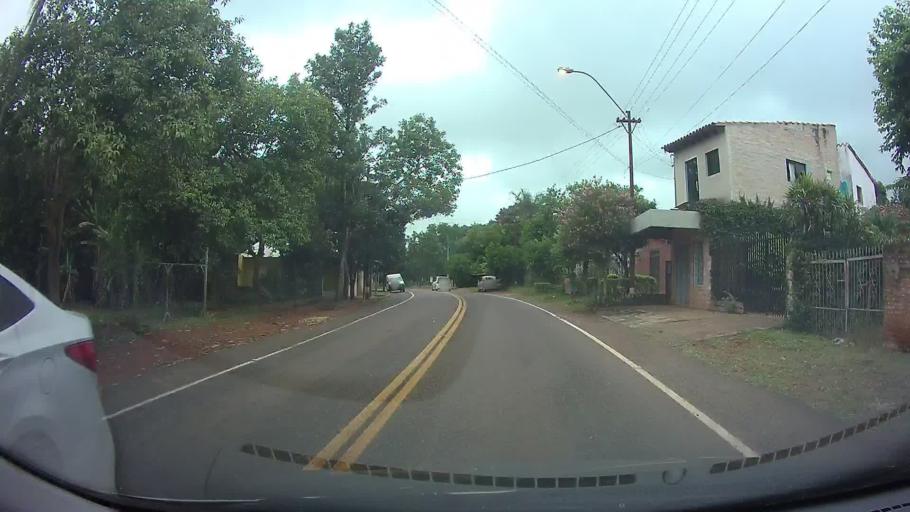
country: PY
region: Paraguari
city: Acahay
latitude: -25.9146
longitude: -57.1150
